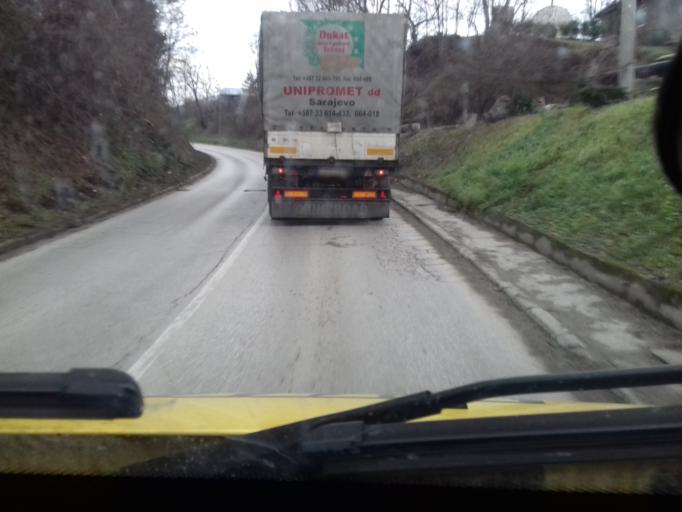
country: BA
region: Federation of Bosnia and Herzegovina
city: Zepce
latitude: 44.4303
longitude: 18.0403
